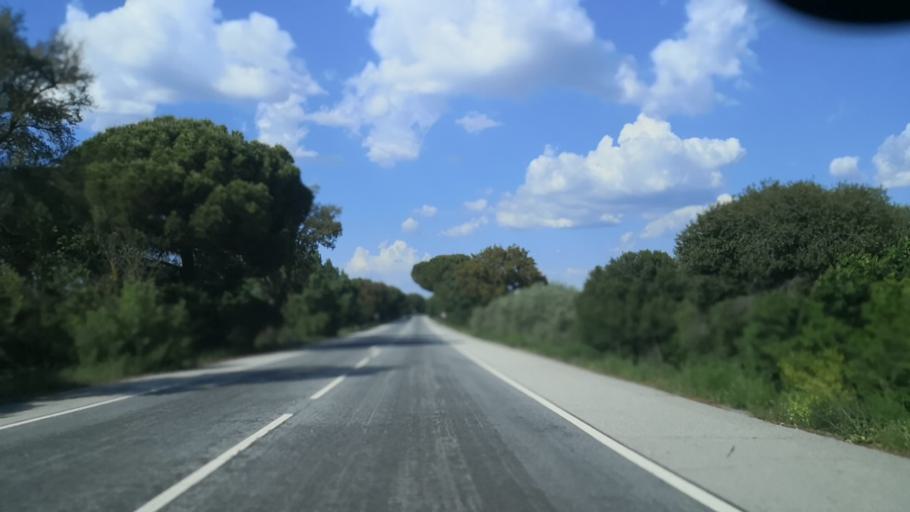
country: PT
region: Evora
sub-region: Arraiolos
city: Arraiolos
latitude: 38.7621
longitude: -7.9299
